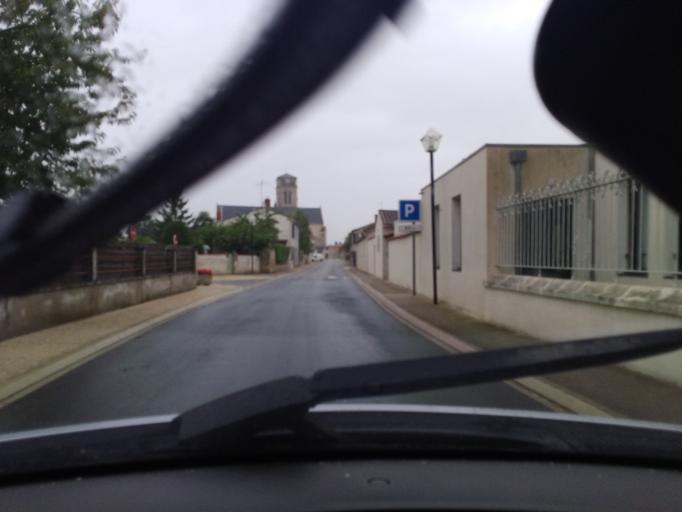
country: FR
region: Pays de la Loire
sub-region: Departement de la Vendee
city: Sainte-Gemme-la-Plaine
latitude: 46.4818
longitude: -1.1150
